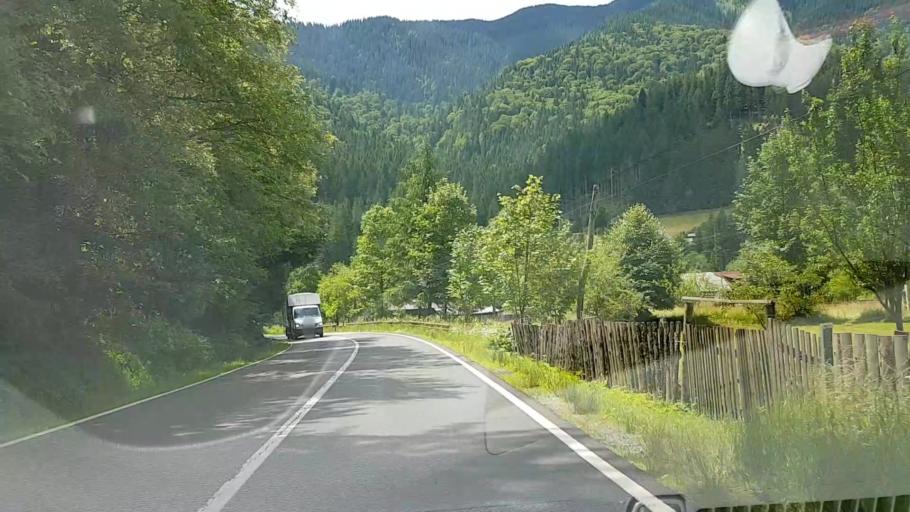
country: RO
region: Suceava
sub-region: Comuna Crucea
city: Crucea
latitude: 47.3833
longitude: 25.5766
